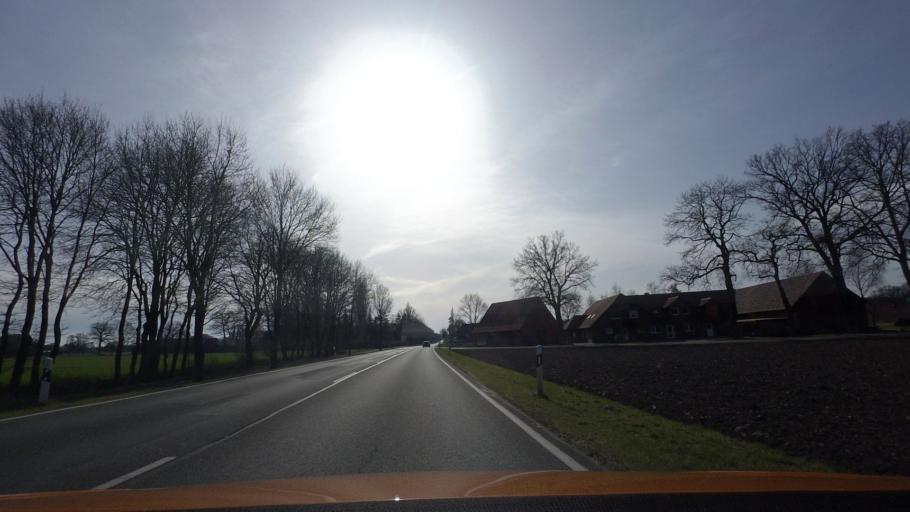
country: DE
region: Lower Saxony
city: Raddestorf
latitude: 52.4523
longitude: 8.9246
